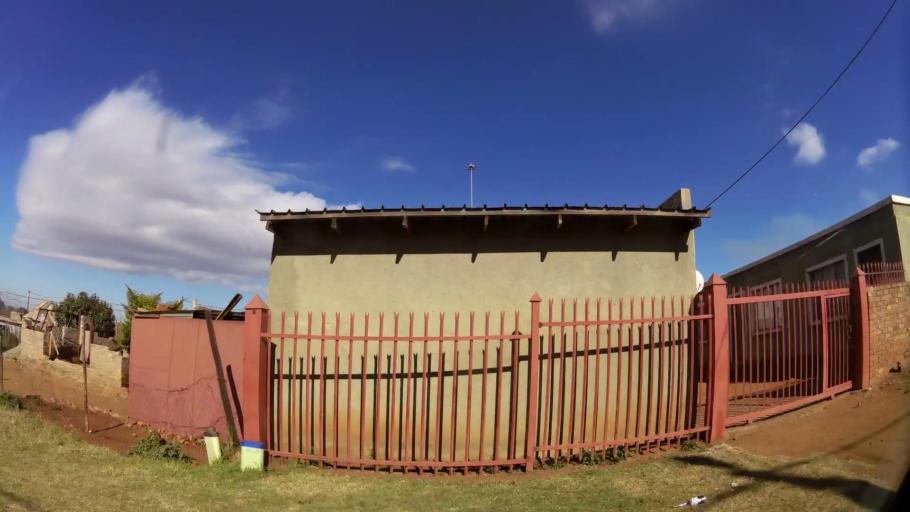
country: ZA
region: Gauteng
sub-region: City of Tshwane Metropolitan Municipality
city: Cullinan
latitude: -25.6964
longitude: 28.4182
